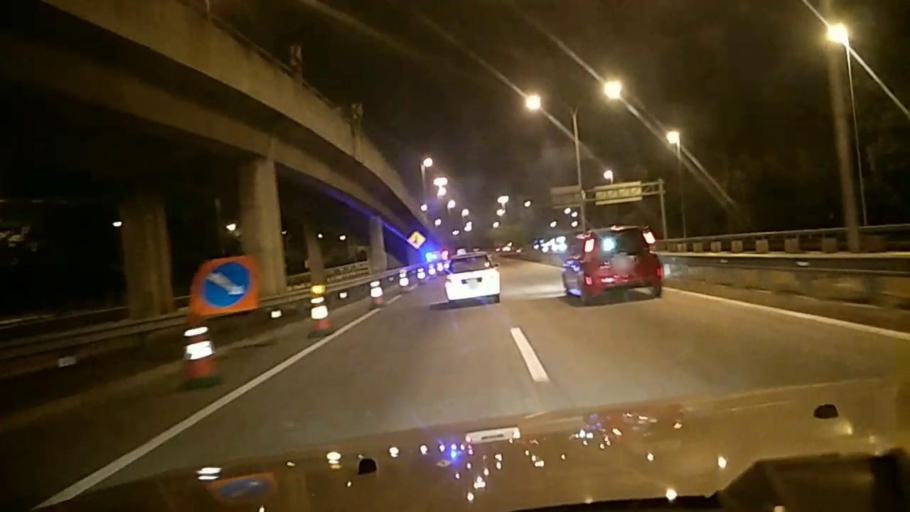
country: MY
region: Penang
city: Perai
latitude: 5.3618
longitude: 100.4031
